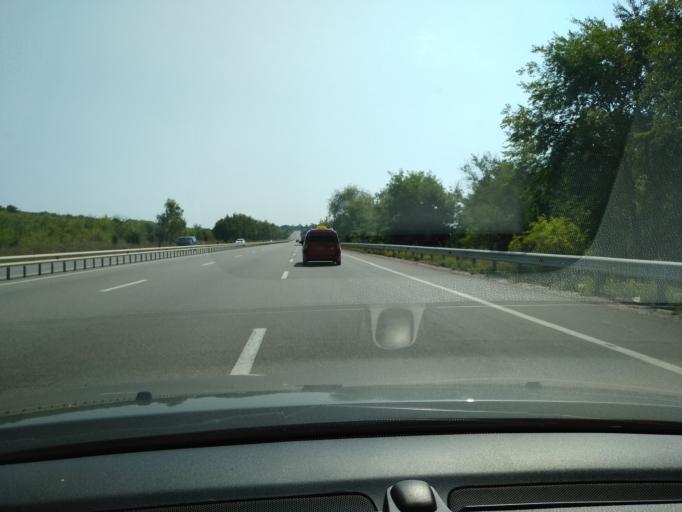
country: MD
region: Chisinau
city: Cricova
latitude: 47.1277
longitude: 28.8476
